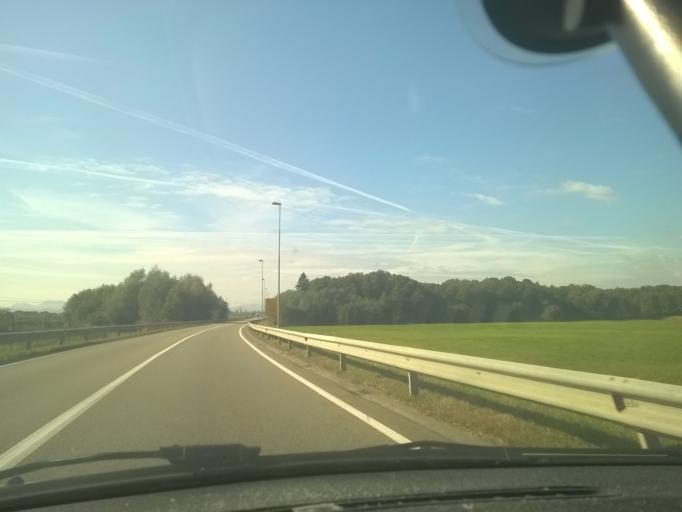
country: SI
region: Ptuj
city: Ptuj
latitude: 46.3990
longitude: 15.8741
